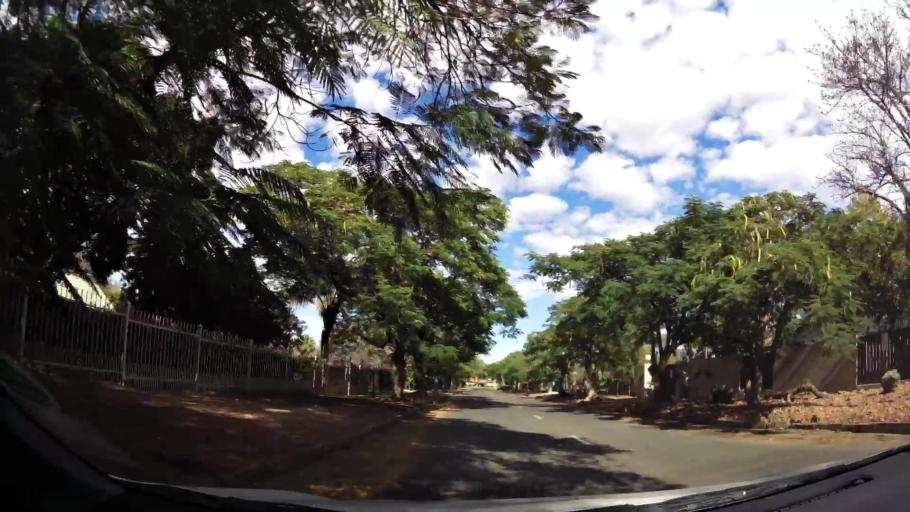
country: ZA
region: Limpopo
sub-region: Waterberg District Municipality
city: Warmbaths
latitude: -24.8761
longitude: 28.2888
